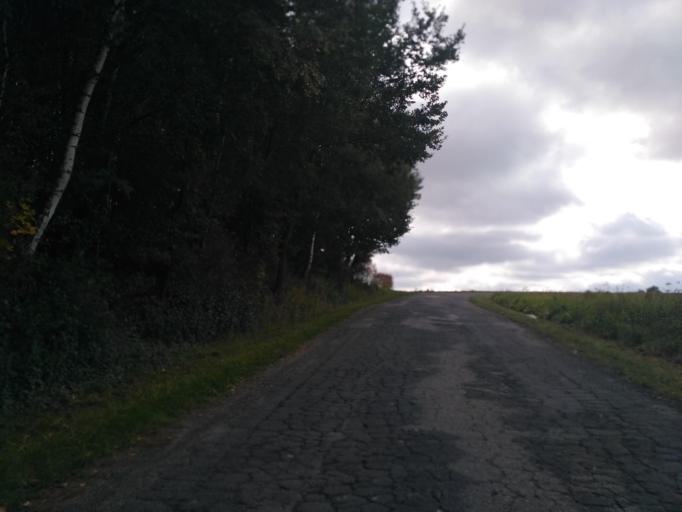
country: PL
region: Subcarpathian Voivodeship
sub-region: Powiat ropczycko-sedziszowski
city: Niedzwiada
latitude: 49.9329
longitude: 21.4704
